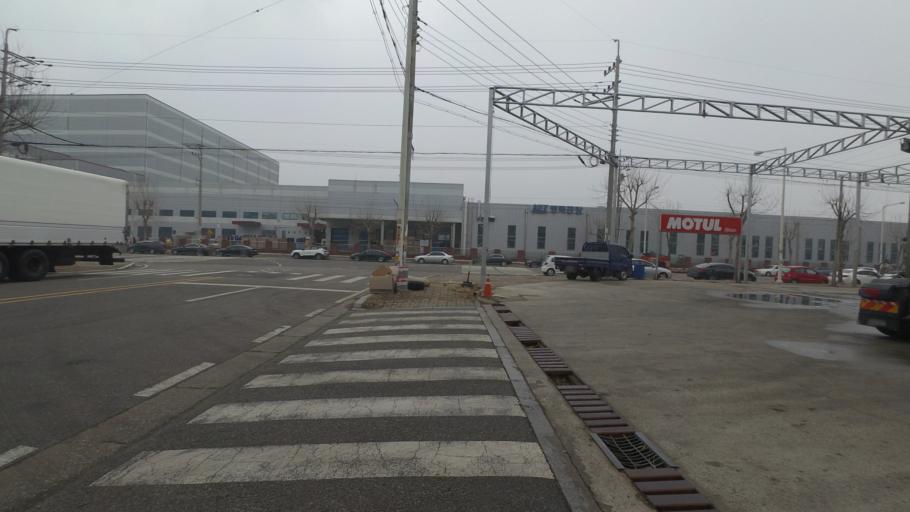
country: KR
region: Chungcheongnam-do
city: Tangjin
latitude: 36.9741
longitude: 126.8461
